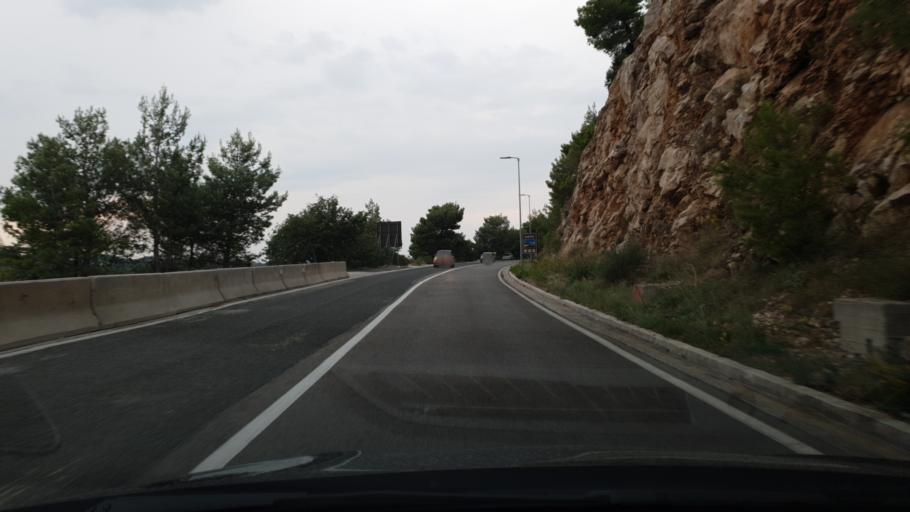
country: HR
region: Dubrovacko-Neretvanska
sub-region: Grad Dubrovnik
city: Mokosica
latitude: 42.6694
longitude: 18.0788
